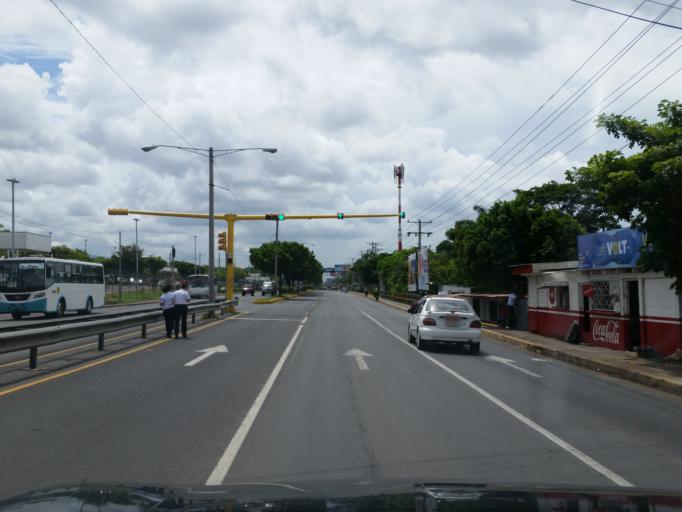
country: NI
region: Managua
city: Managua
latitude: 12.1453
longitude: -86.1694
